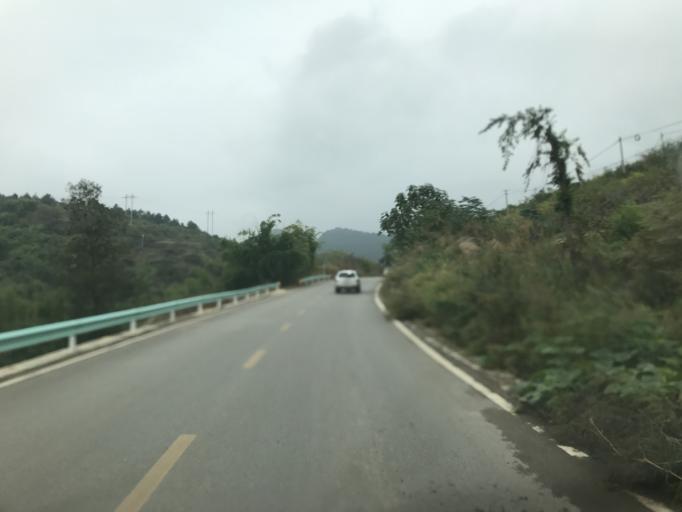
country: CN
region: Guizhou Sheng
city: Guiyang
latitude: 26.7079
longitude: 106.8848
